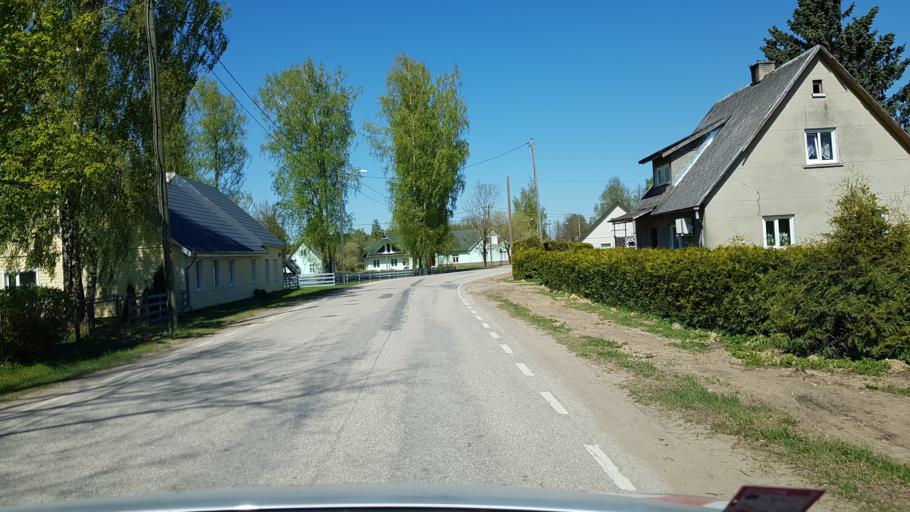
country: EE
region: Vorumaa
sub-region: Antsla vald
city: Vana-Antsla
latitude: 57.8239
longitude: 26.5236
